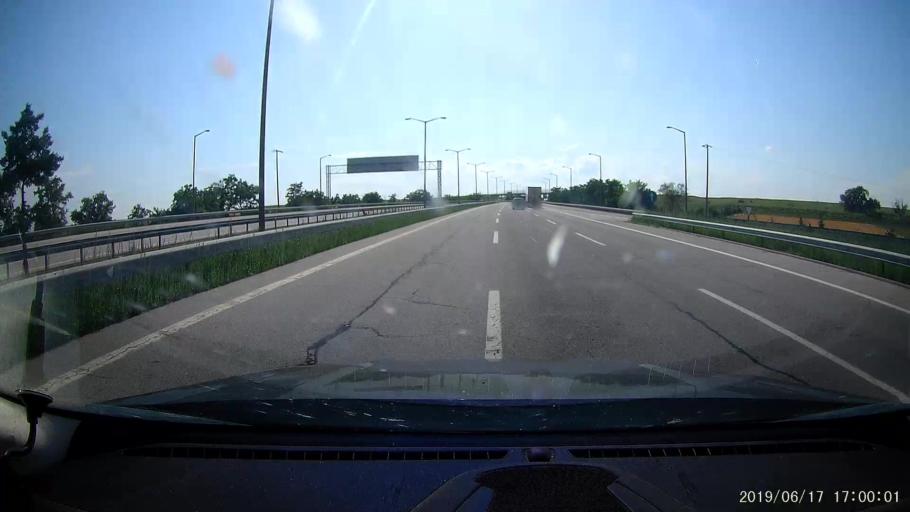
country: TR
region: Edirne
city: Haskoy
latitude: 41.6192
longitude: 26.8430
